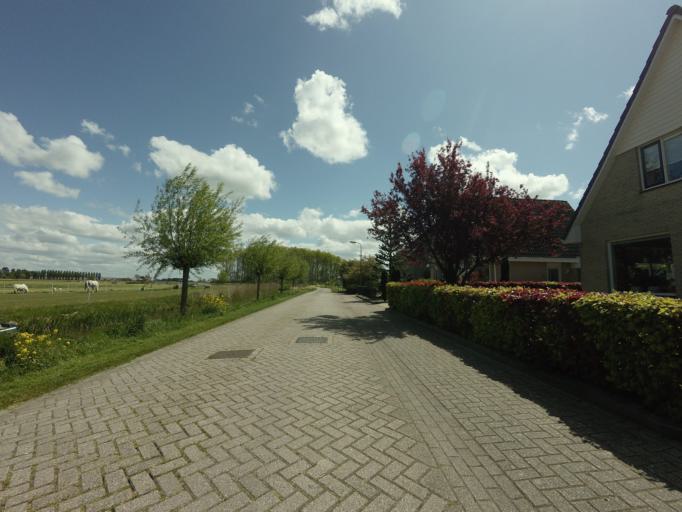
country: NL
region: Friesland
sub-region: Gemeente Franekeradeel
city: Franeker
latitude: 53.1480
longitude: 5.4893
